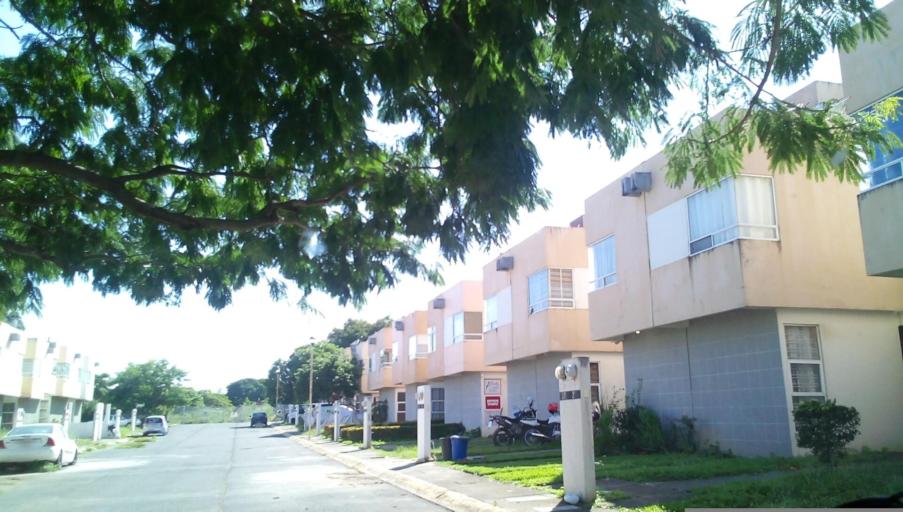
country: MX
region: Veracruz
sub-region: Veracruz
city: Lomas de Rio Medio Cuatro
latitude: 19.1769
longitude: -96.2103
